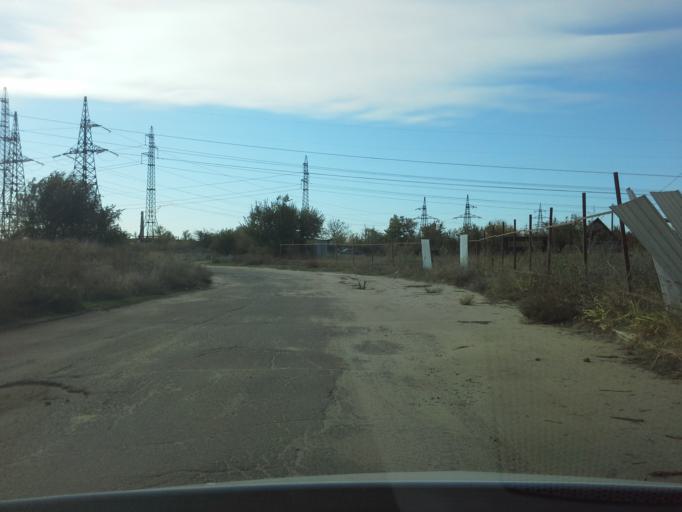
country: RU
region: Volgograd
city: Vodstroy
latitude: 48.8386
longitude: 44.6291
